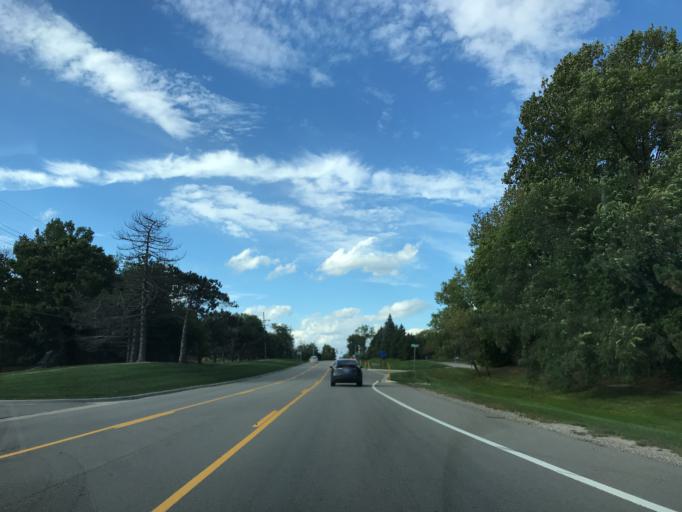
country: US
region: Michigan
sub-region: Oakland County
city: Farmington Hills
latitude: 42.5242
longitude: -83.3992
